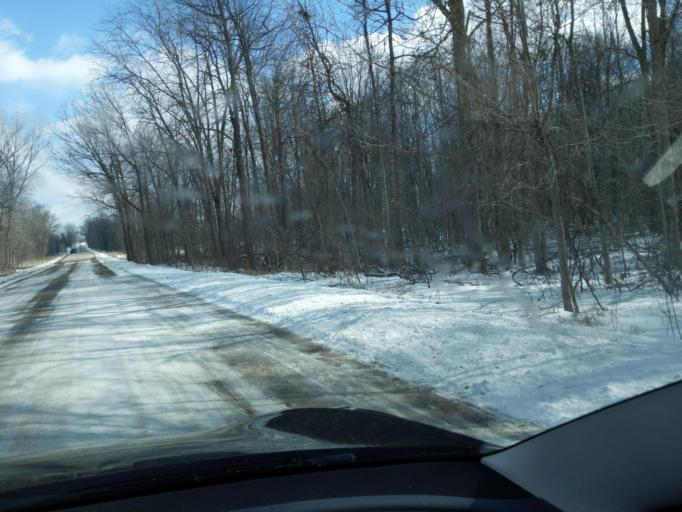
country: US
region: Michigan
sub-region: Livingston County
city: Fowlerville
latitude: 42.6139
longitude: -84.0835
